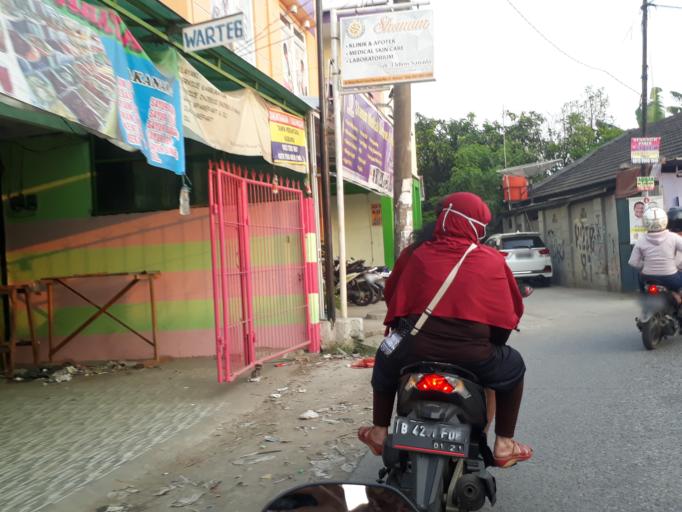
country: ID
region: West Java
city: Bekasi
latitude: -6.2435
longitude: 107.0454
